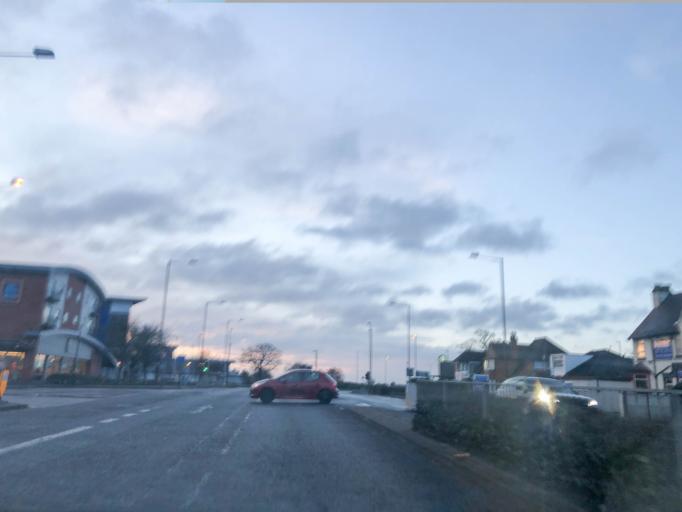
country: GB
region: England
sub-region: Solihull
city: Tidbury Green
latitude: 52.4060
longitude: -1.8875
